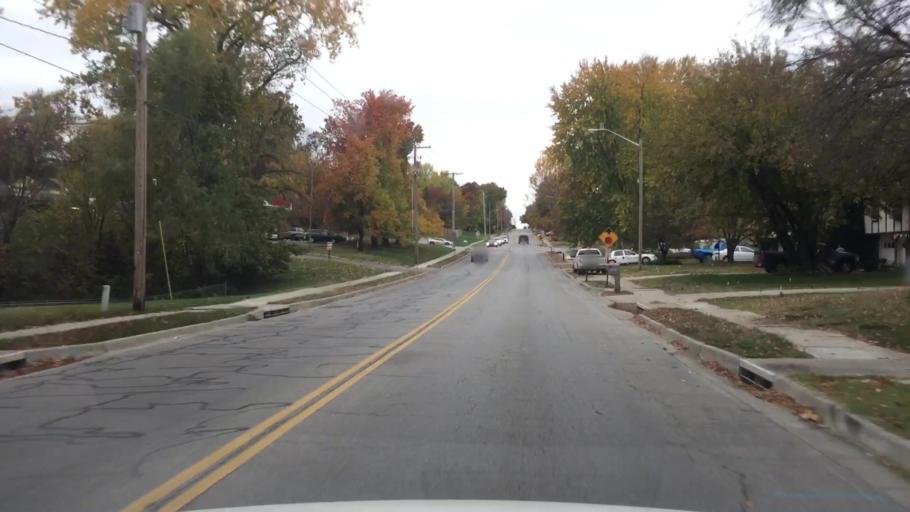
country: US
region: Kansas
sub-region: Johnson County
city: Shawnee
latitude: 39.0440
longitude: -94.7035
